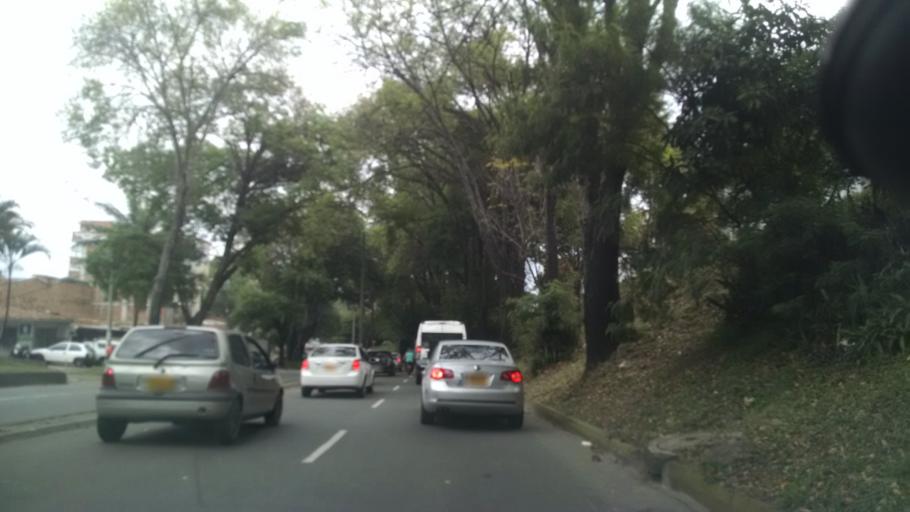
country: CO
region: Antioquia
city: Medellin
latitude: 6.2531
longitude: -75.6005
